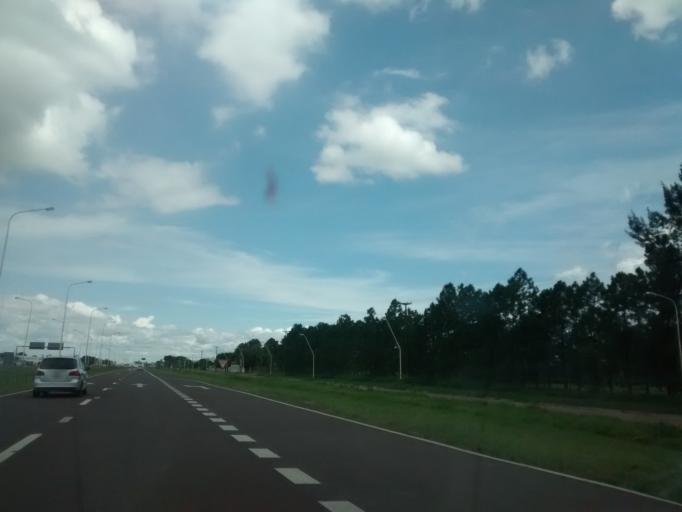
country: AR
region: Chaco
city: Resistencia
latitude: -27.4121
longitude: -58.9746
